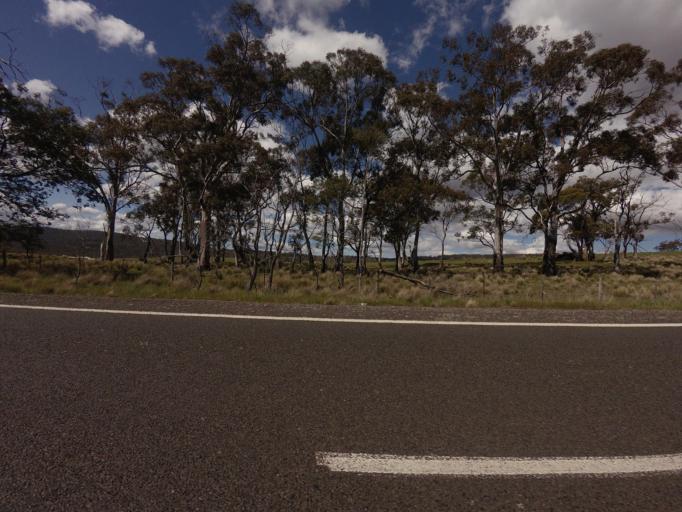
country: AU
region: Tasmania
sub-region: Northern Midlands
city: Evandale
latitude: -41.9428
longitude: 147.6039
